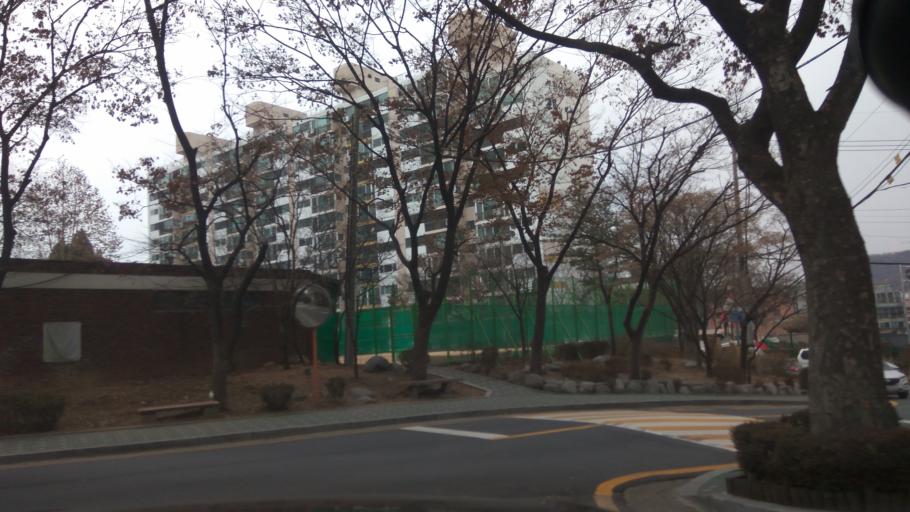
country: KR
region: Incheon
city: Incheon
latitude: 37.4949
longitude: 126.7075
